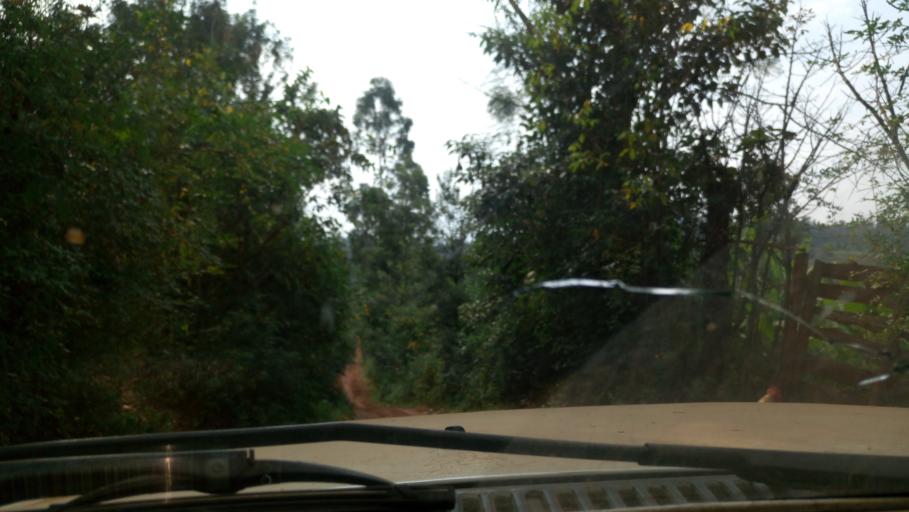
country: KE
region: Murang'a District
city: Maragua
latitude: -0.8062
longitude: 37.0327
